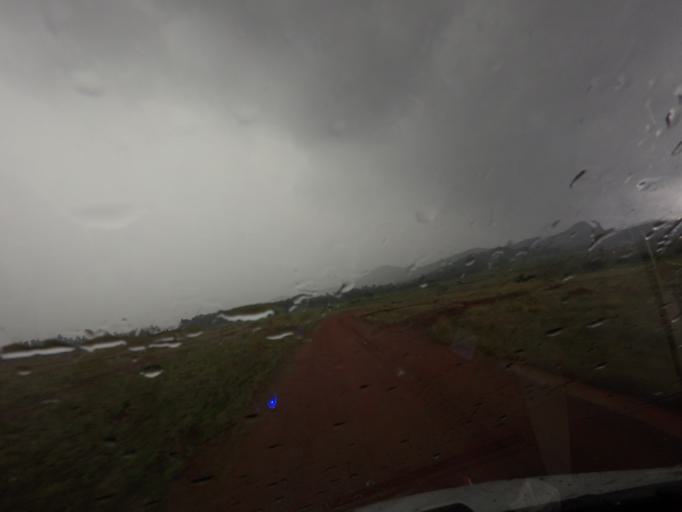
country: SZ
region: Hhohho
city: Lobamba
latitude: -26.4790
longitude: 31.1936
